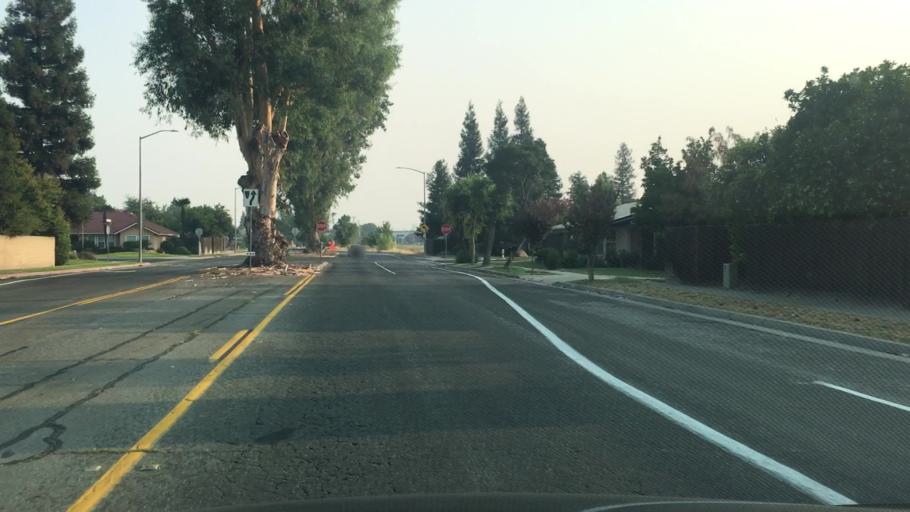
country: US
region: California
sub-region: Fresno County
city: Clovis
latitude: 36.8328
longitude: -119.6730
